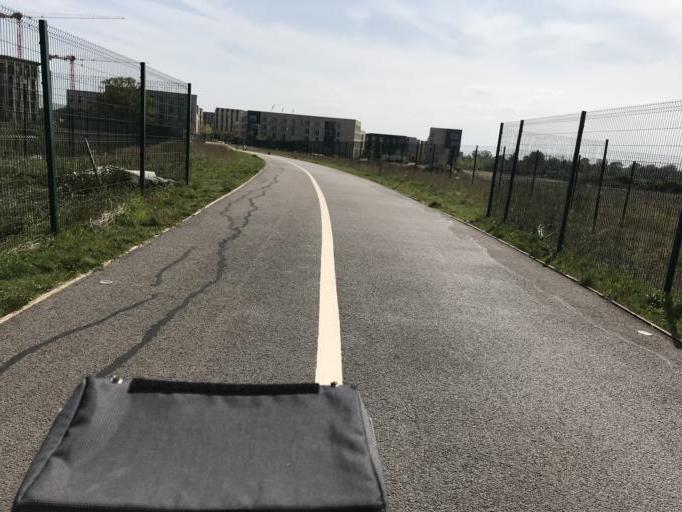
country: GB
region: England
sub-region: Cambridgeshire
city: Girton
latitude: 52.2217
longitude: 0.0844
